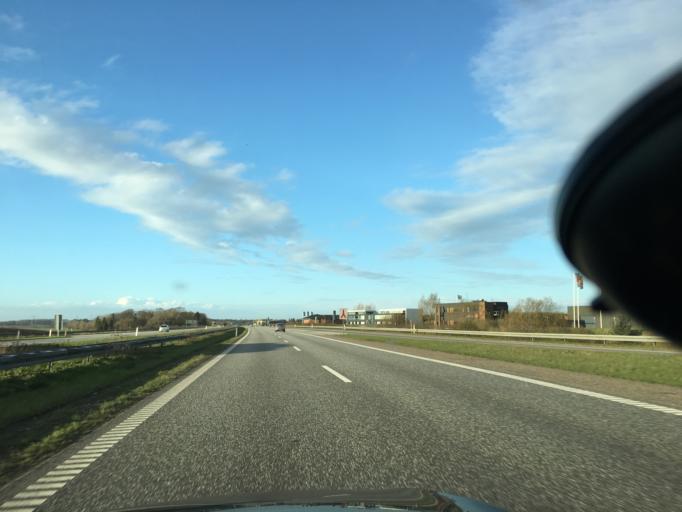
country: DK
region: North Denmark
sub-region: Rebild Kommune
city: Stovring
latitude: 56.8810
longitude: 9.8046
